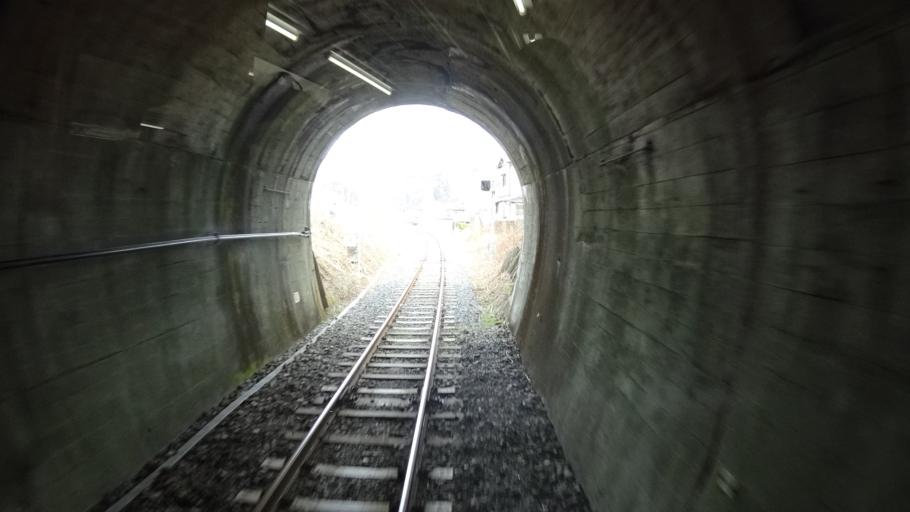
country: JP
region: Iwate
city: Miyako
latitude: 39.6344
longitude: 141.9614
